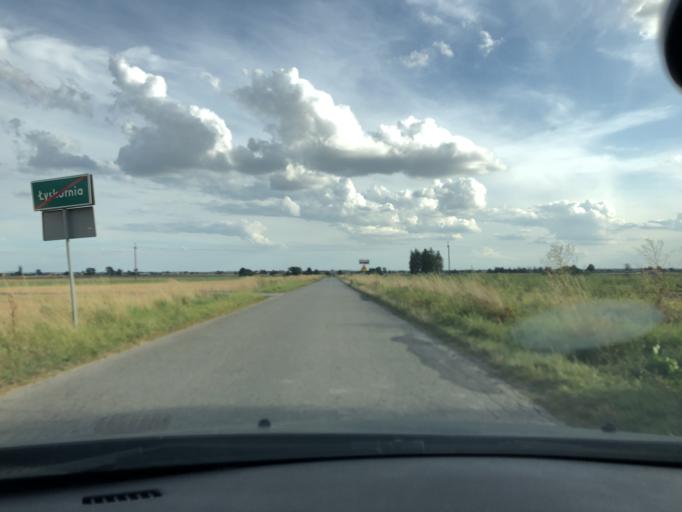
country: PL
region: Lodz Voivodeship
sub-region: Powiat wieruszowski
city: Walichnowy
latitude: 51.2594
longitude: 18.3942
